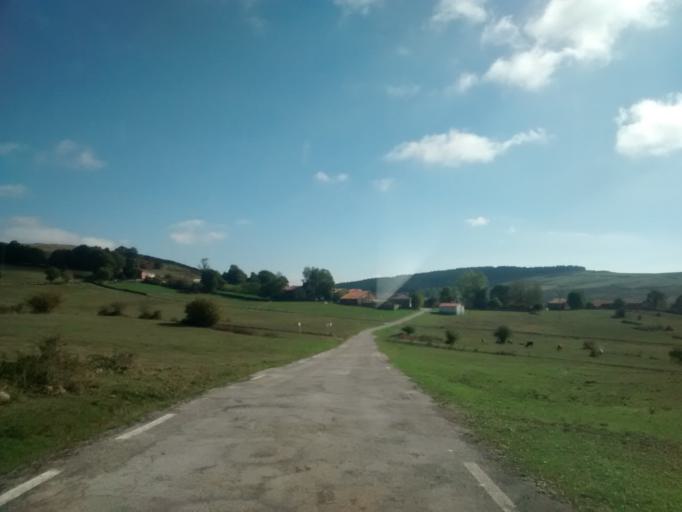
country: ES
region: Castille and Leon
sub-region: Provincia de Burgos
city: Arija
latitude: 42.9267
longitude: -4.0049
